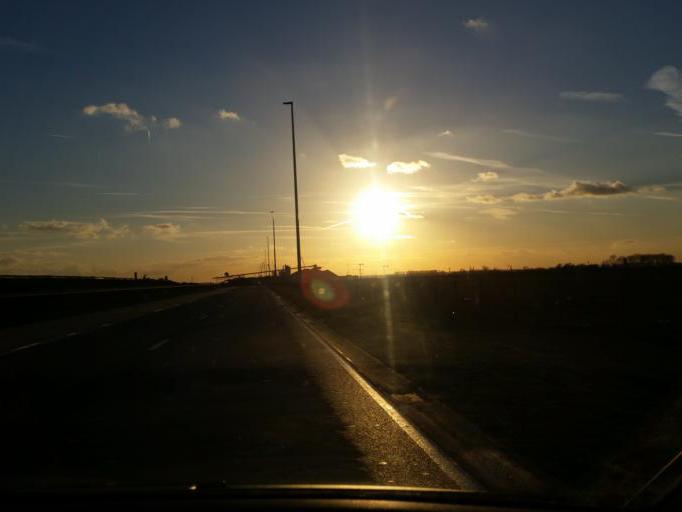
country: BE
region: Flanders
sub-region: Provincie Oost-Vlaanderen
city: Beveren
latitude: 51.2973
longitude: 4.2422
